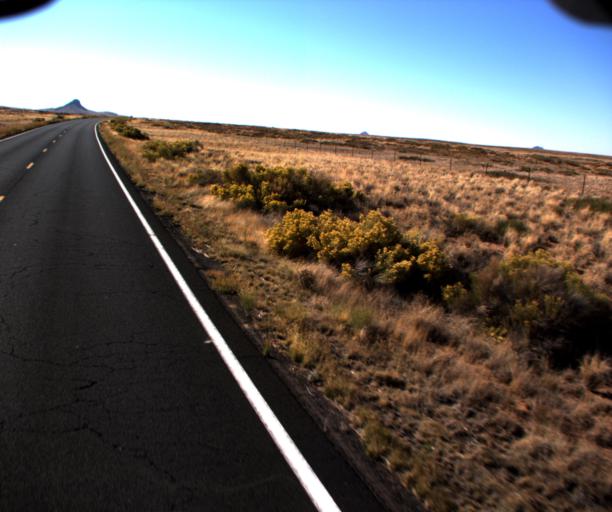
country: US
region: Arizona
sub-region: Navajo County
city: Dilkon
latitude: 35.4656
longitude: -110.4226
